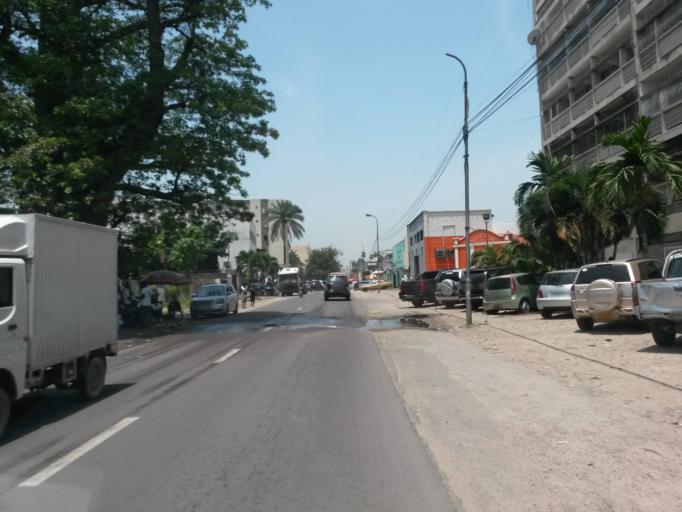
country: CD
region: Kinshasa
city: Kinshasa
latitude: -4.2992
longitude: 15.3168
